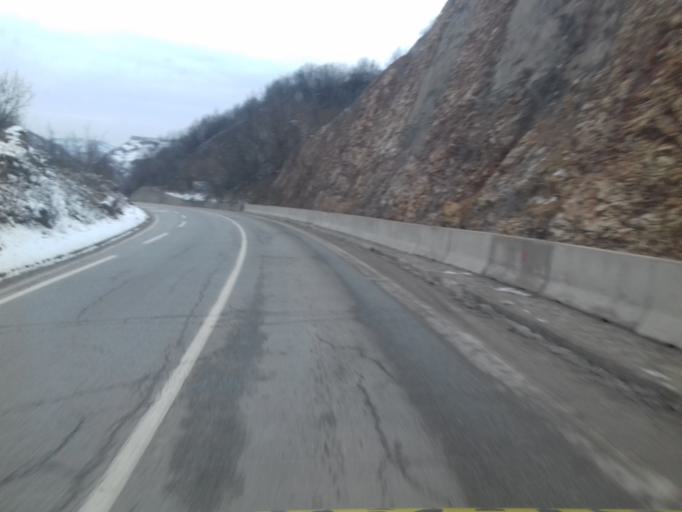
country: BA
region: Federation of Bosnia and Herzegovina
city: Kobilja Glava
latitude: 43.8533
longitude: 18.4628
